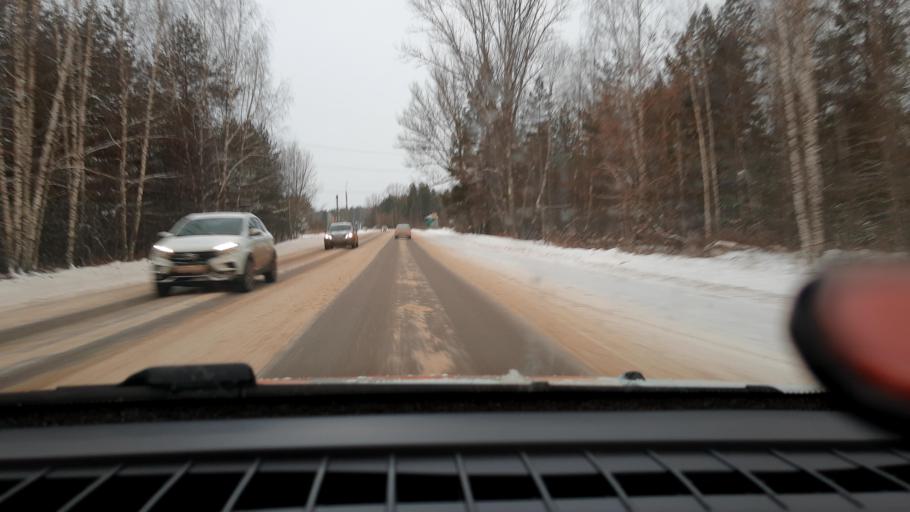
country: RU
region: Nizjnij Novgorod
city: Afonino
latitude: 56.3229
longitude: 44.1470
